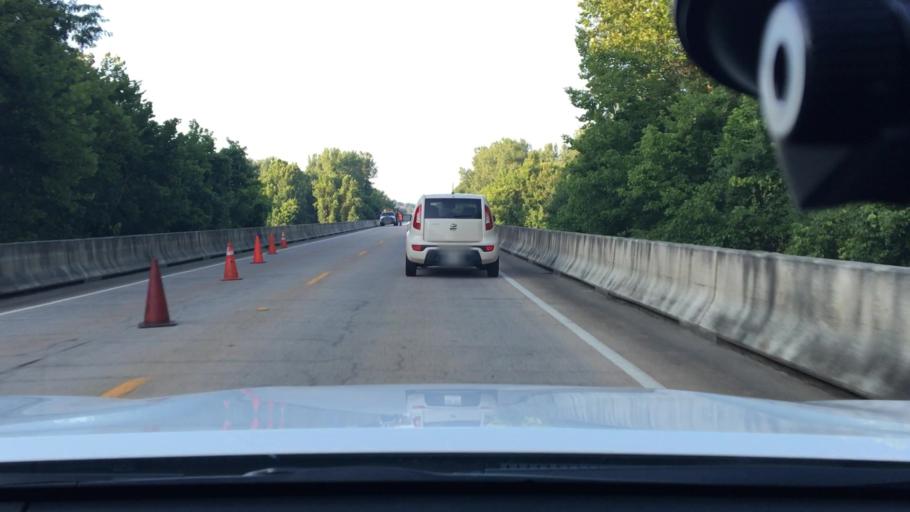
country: US
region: Arkansas
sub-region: Johnson County
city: Clarksville
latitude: 35.4007
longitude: -93.5311
